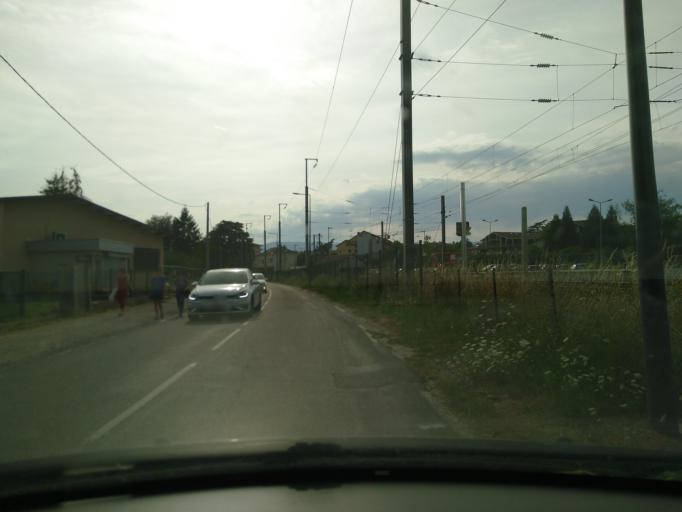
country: FR
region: Rhone-Alpes
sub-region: Departement de la Haute-Savoie
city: Saint-Julien-en-Genevois
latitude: 46.1421
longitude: 6.0880
